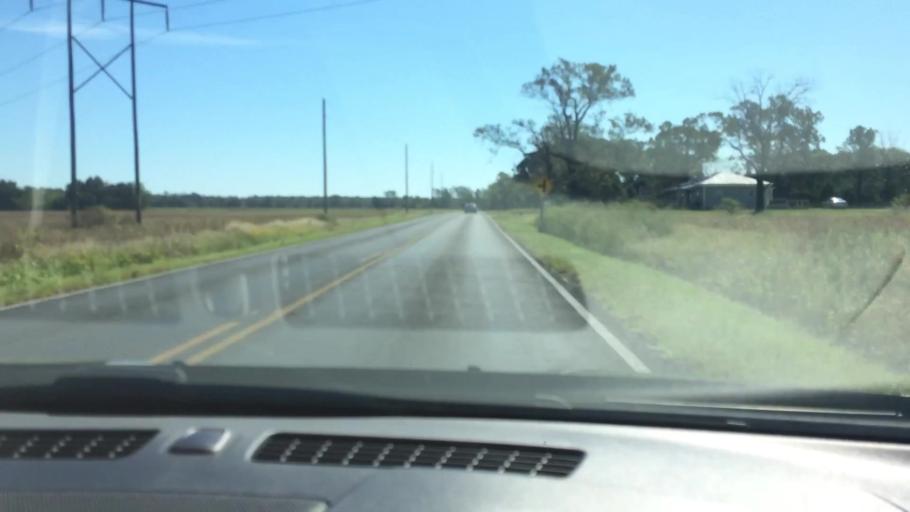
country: US
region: North Carolina
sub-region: Pitt County
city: Grifton
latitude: 35.3711
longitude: -77.3554
